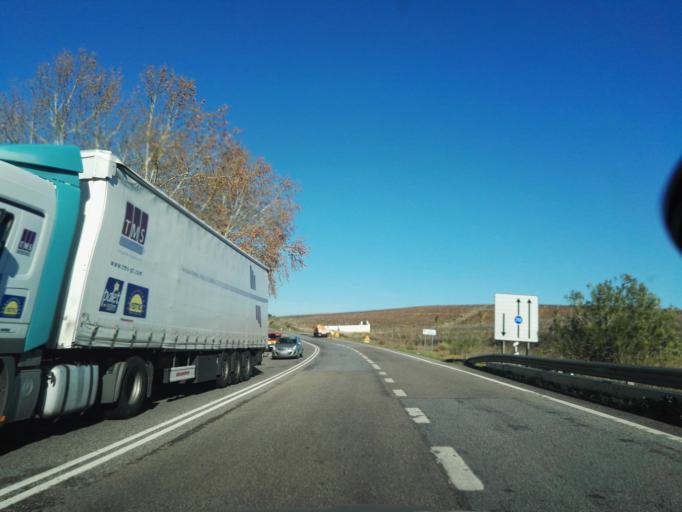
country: PT
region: Evora
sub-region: Vila Vicosa
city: Vila Vicosa
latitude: 38.8318
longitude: -7.4045
